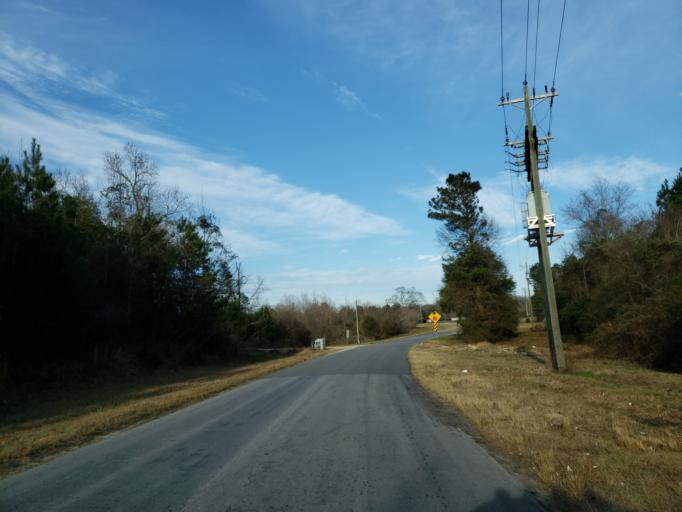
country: US
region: Mississippi
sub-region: Wayne County
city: Belmont
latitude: 31.5084
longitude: -88.5059
